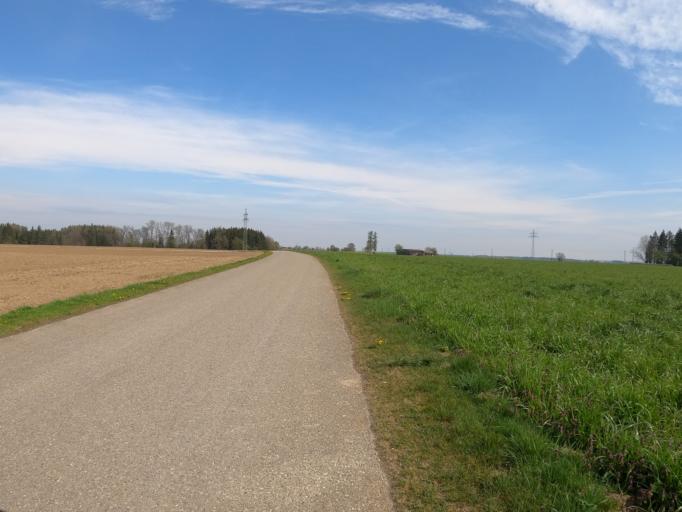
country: DE
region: Bavaria
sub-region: Swabia
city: Rieden an der Kotz
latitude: 48.3712
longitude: 10.2185
